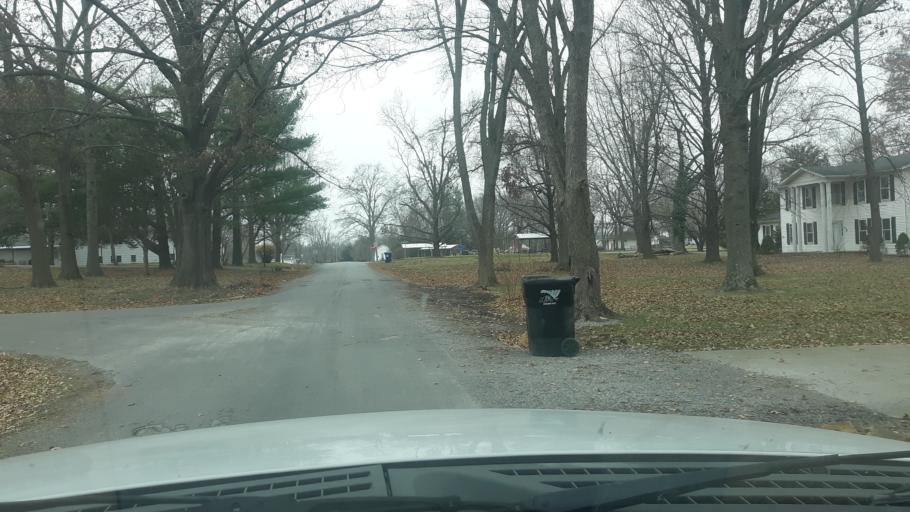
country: US
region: Illinois
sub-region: Saline County
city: Harrisburg
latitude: 37.8376
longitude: -88.6079
